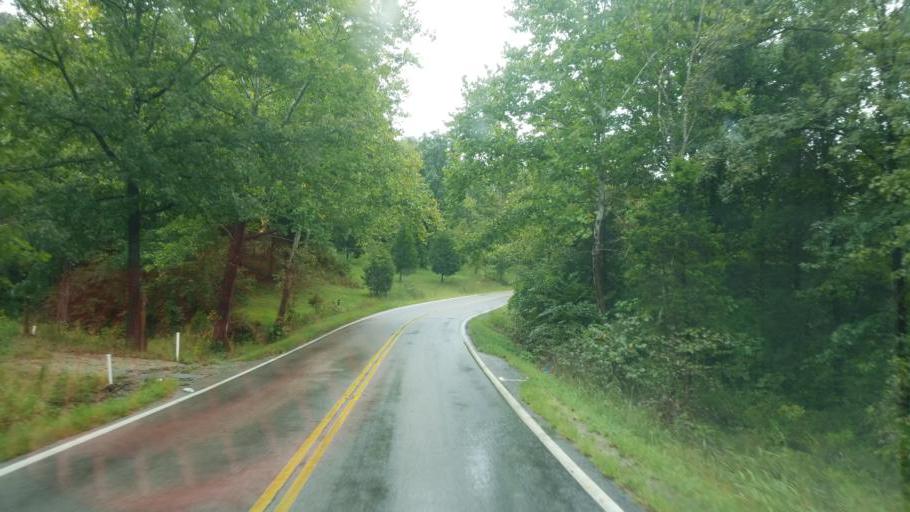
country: US
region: Ohio
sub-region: Adams County
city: West Union
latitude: 38.7863
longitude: -83.5395
